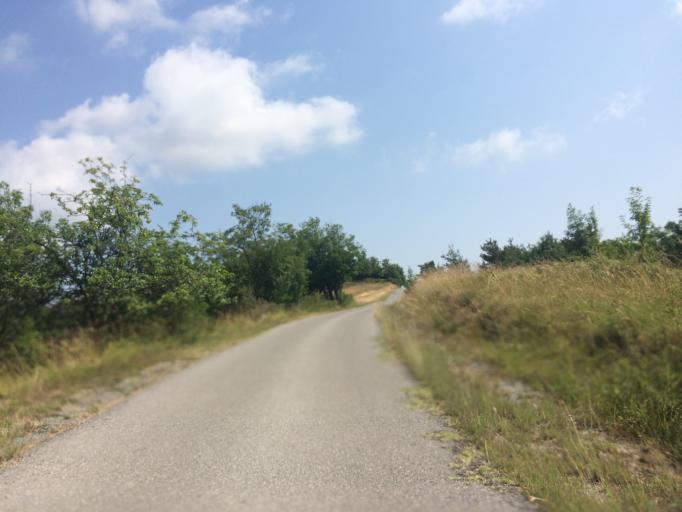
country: IT
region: Piedmont
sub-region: Provincia di Alessandria
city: Pareto
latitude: 44.4990
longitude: 8.3667
